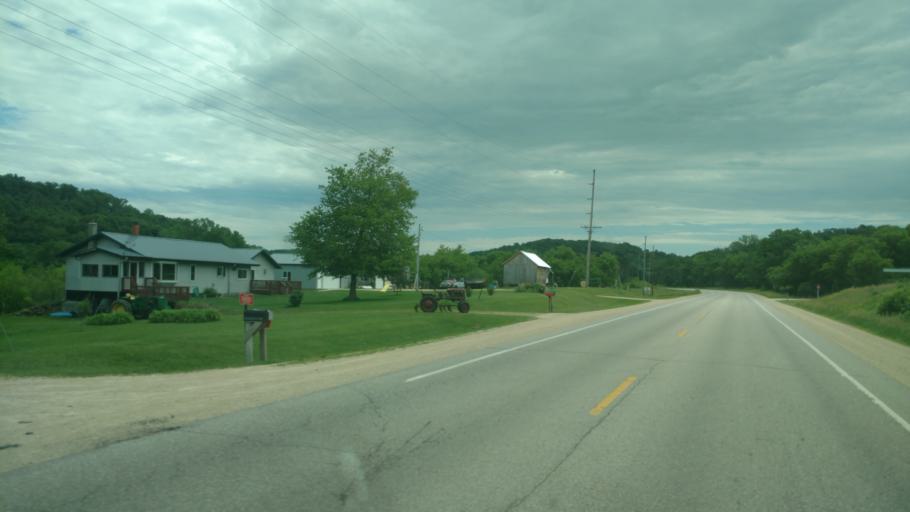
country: US
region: Wisconsin
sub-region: Monroe County
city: Tomah
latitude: 43.8260
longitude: -90.4537
